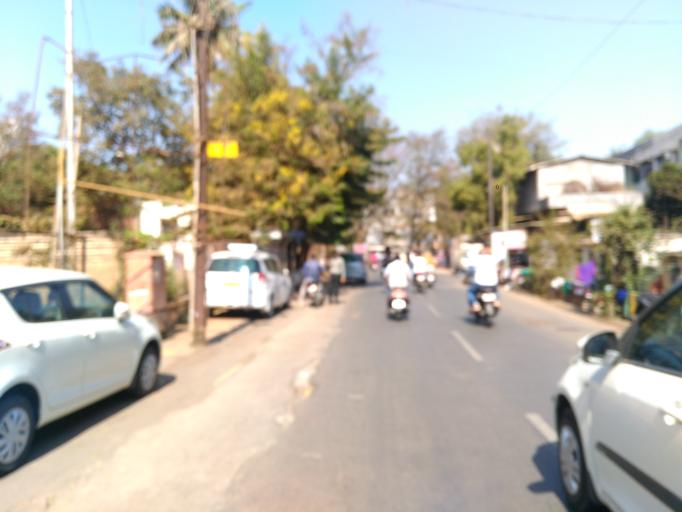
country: IN
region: Maharashtra
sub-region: Pune Division
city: Pune
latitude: 18.4954
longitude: 73.8497
